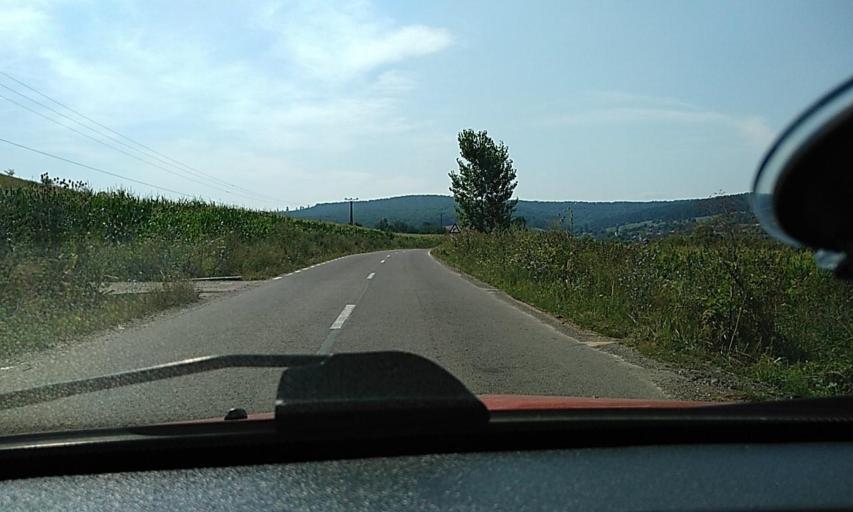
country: RO
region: Brasov
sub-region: Oras Rupea
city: Fiser
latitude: 46.0190
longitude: 25.1508
